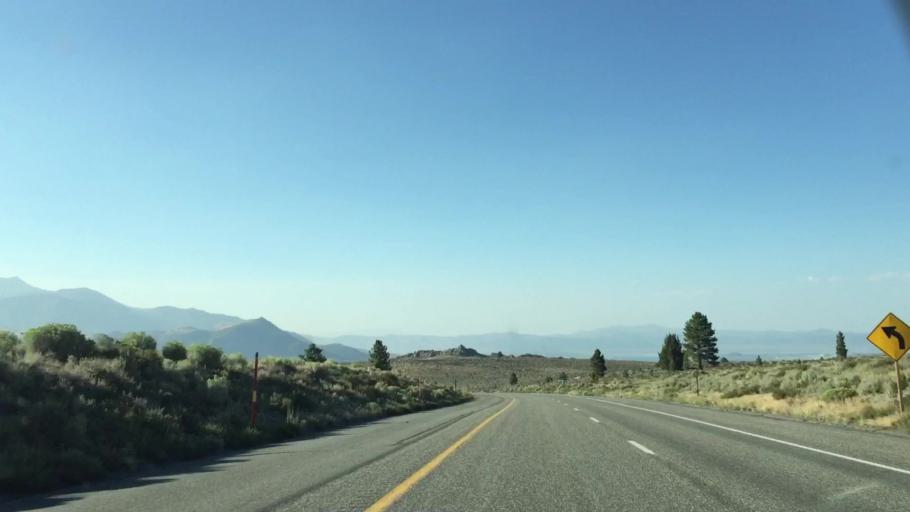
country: US
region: California
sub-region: Mono County
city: Mammoth Lakes
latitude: 37.8368
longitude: -119.0699
